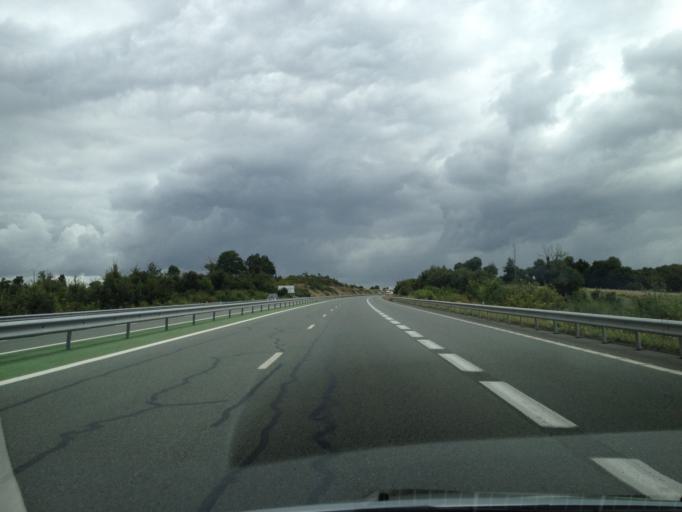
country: FR
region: Pays de la Loire
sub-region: Departement de la Vendee
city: La Gaubretiere
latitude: 46.9159
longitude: -1.0410
